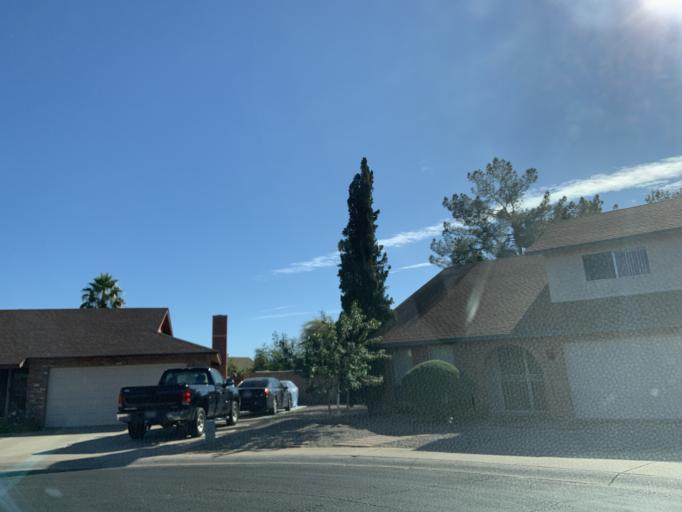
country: US
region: Arizona
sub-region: Maricopa County
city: San Carlos
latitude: 33.3750
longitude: -111.8612
